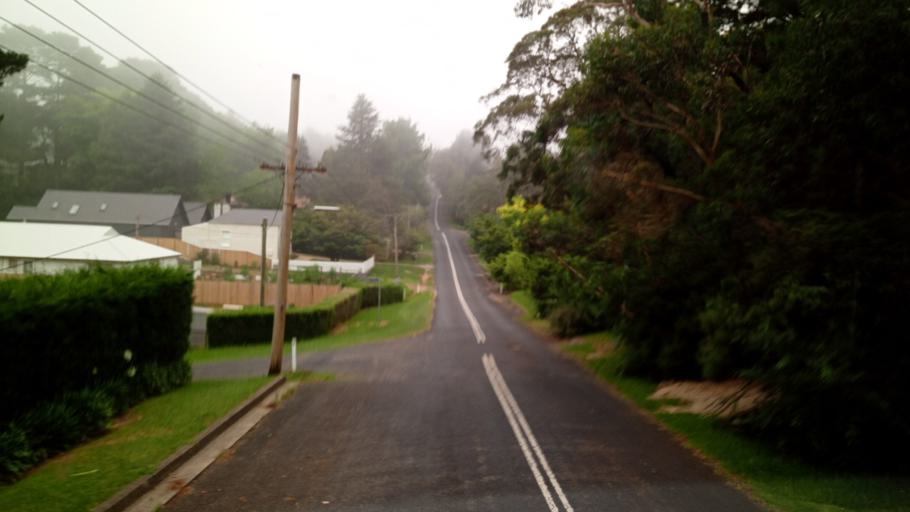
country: AU
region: New South Wales
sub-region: Blue Mountains Municipality
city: Leura
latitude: -33.7199
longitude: 150.3388
